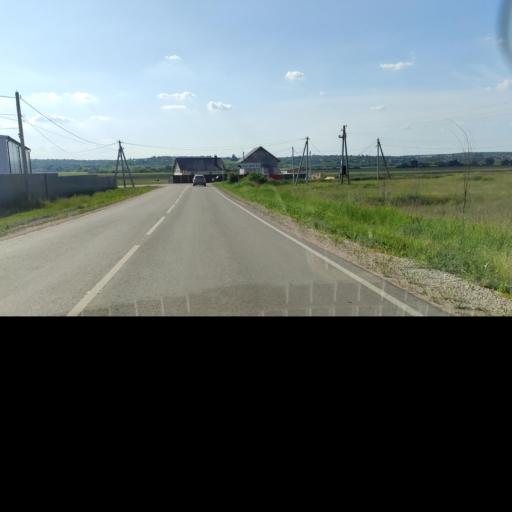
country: RU
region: Voronezj
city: Podgornoye
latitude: 51.8535
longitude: 39.1523
